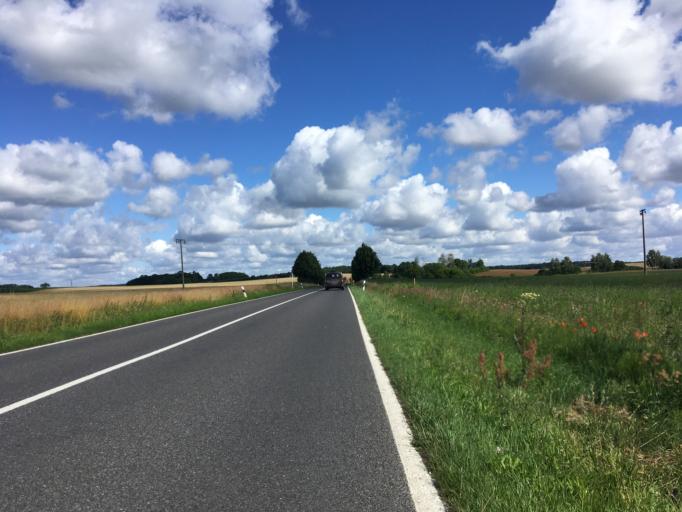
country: DE
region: Brandenburg
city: Templin
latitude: 53.1729
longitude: 13.5628
